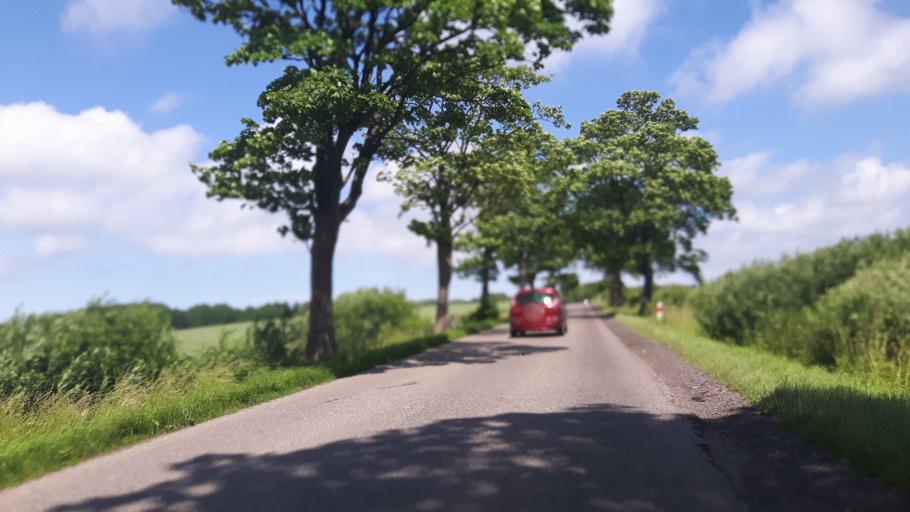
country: PL
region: Pomeranian Voivodeship
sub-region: Powiat slupski
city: Ustka
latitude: 54.5284
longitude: 16.8131
